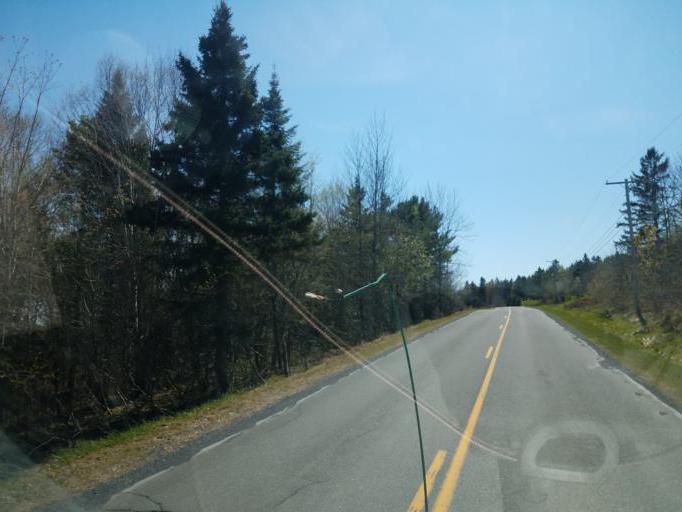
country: US
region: Maine
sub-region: Aroostook County
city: Caribou
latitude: 46.9478
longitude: -68.1062
